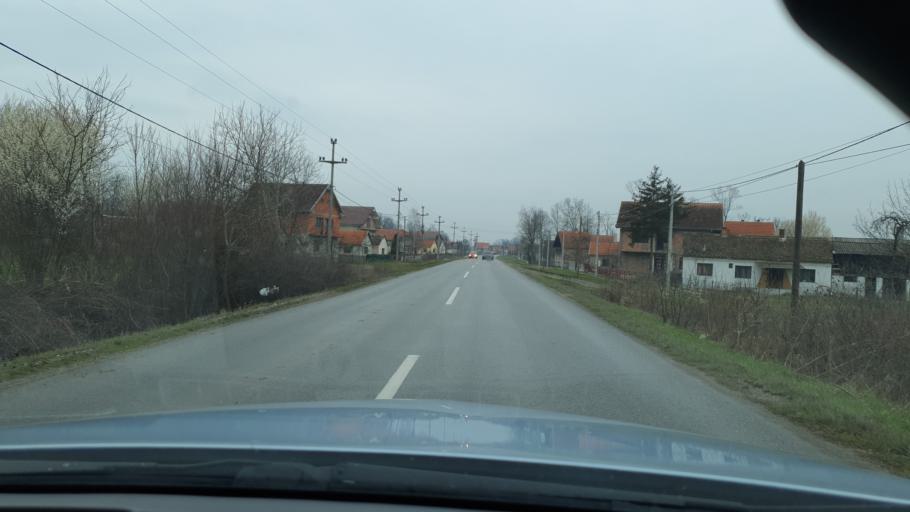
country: RS
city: Belotic
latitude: 44.8016
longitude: 19.5598
